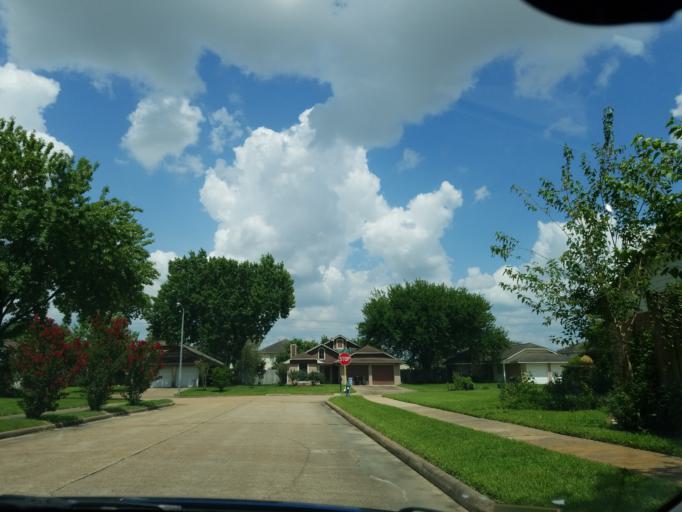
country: US
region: Texas
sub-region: Harris County
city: Cypress
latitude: 29.8736
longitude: -95.7299
